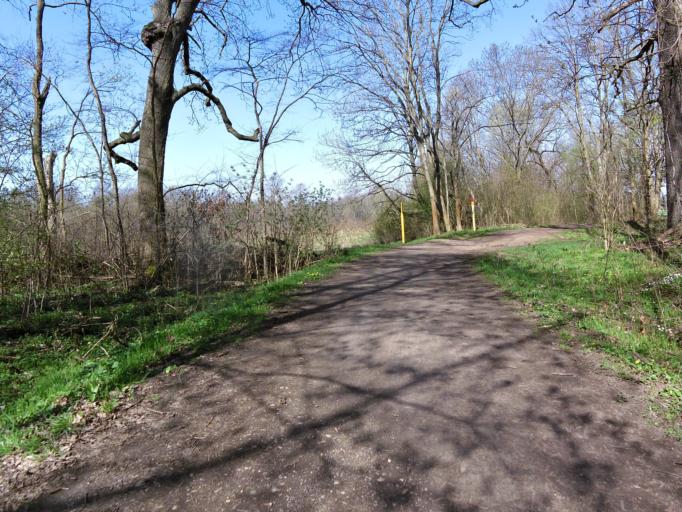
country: DE
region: Saxony
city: Schkeuditz
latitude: 51.3691
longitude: 12.2766
